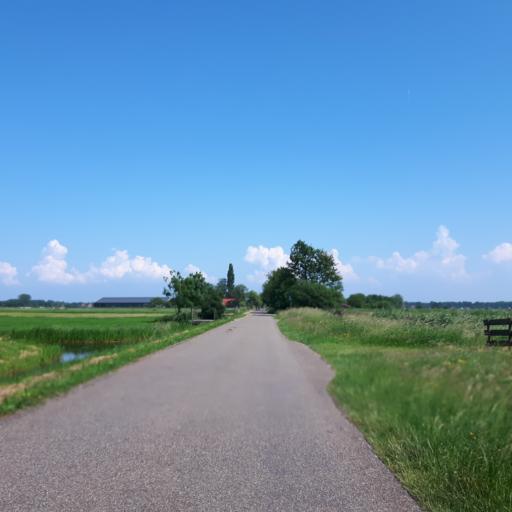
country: NL
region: Utrecht
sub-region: Gemeente Utrecht
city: Utrecht
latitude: 52.1391
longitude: 5.1239
